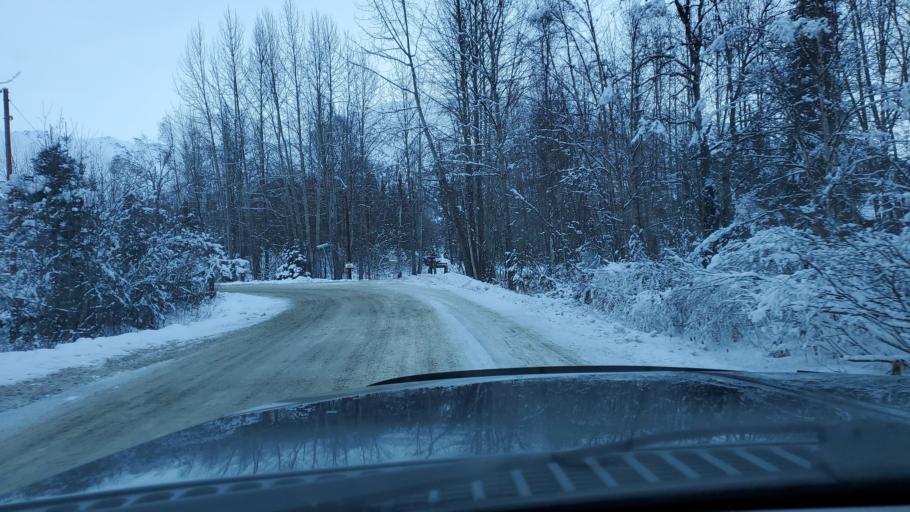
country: US
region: Alaska
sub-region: Matanuska-Susitna Borough
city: Fishhook
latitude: 61.6929
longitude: -149.2998
